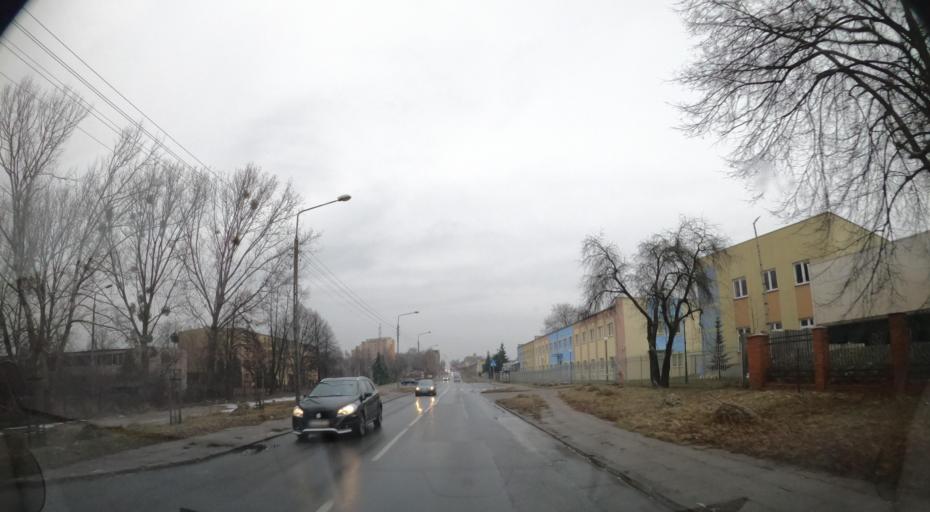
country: PL
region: Masovian Voivodeship
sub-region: Powiat radomski
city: Trablice
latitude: 51.3831
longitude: 21.1216
